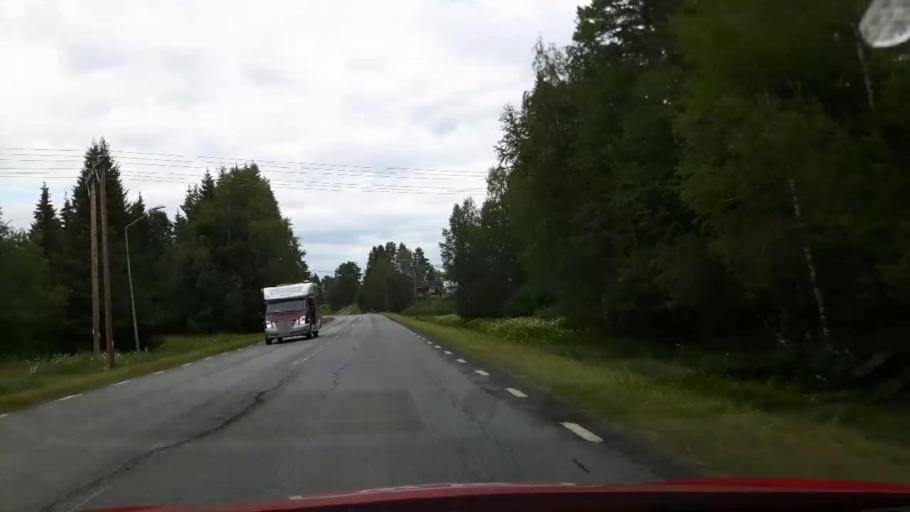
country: SE
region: Jaemtland
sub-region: Stroemsunds Kommun
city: Stroemsund
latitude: 63.5955
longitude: 15.3557
